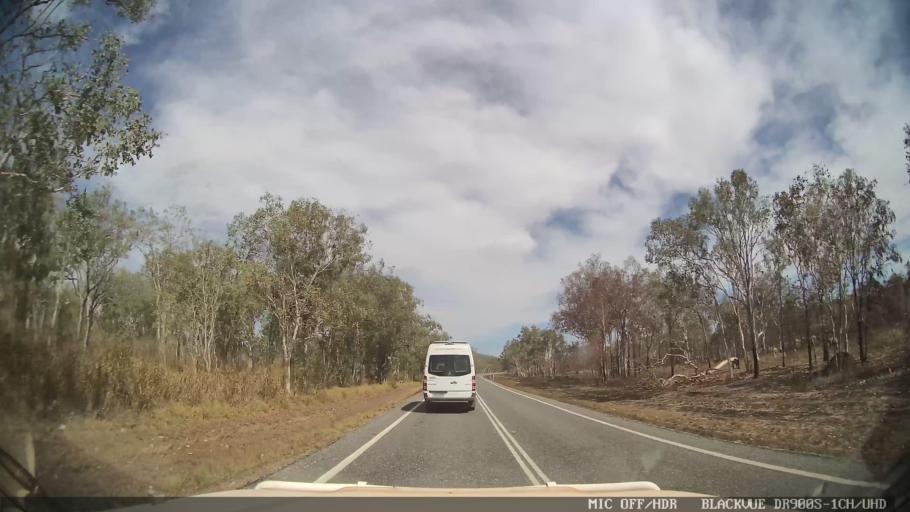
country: AU
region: Queensland
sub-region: Cairns
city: Port Douglas
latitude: -16.7201
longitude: 145.3529
